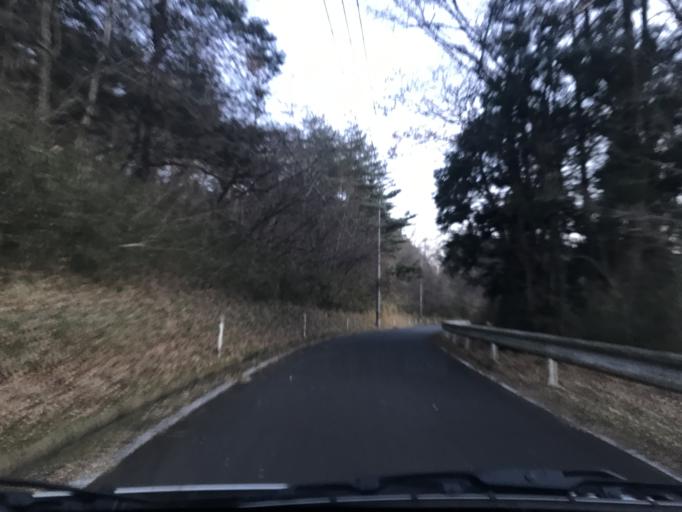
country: JP
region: Iwate
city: Ichinoseki
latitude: 38.8318
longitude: 141.0861
